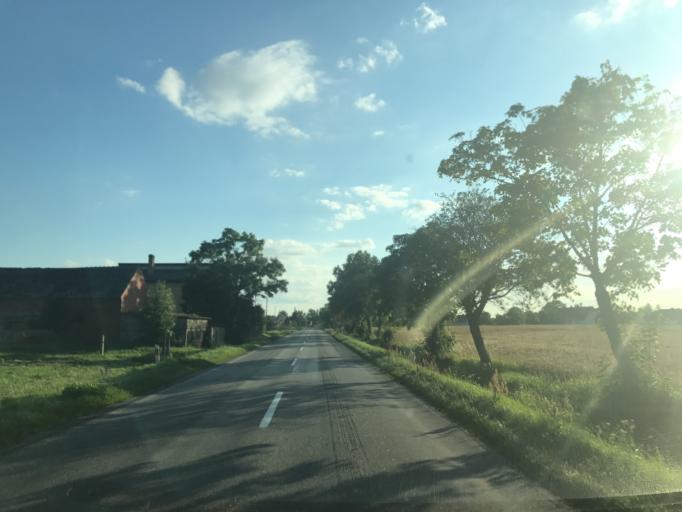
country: PL
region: Greater Poland Voivodeship
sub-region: Powiat jarocinski
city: Kotlin
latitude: 51.9984
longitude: 17.6681
